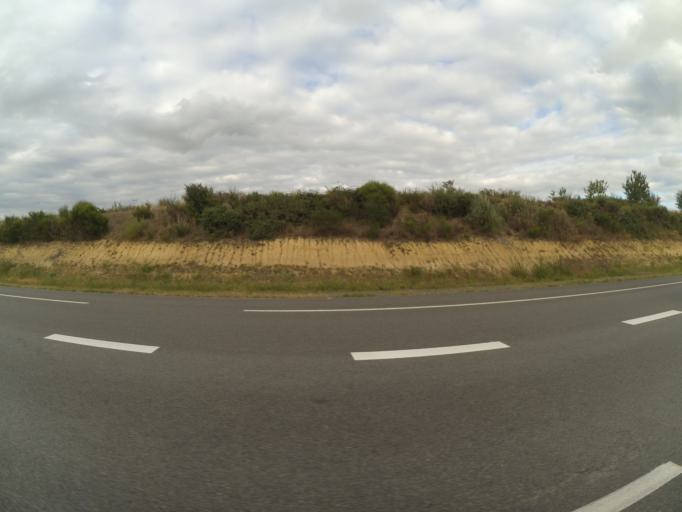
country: FR
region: Pays de la Loire
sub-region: Departement de la Vendee
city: Saligny
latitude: 46.7992
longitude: -1.4307
